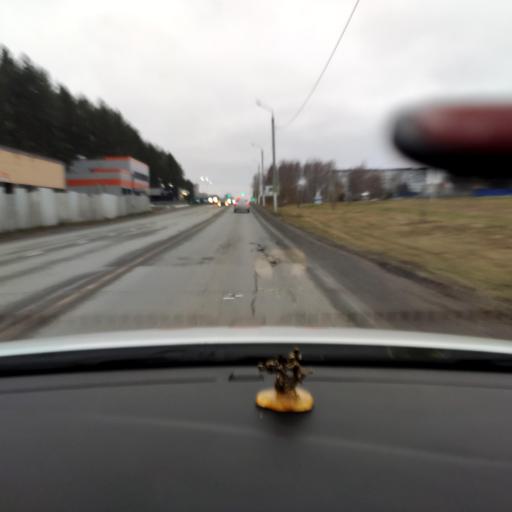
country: RU
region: Tatarstan
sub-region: Zelenodol'skiy Rayon
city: Zelenodolsk
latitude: 55.8533
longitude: 48.5713
